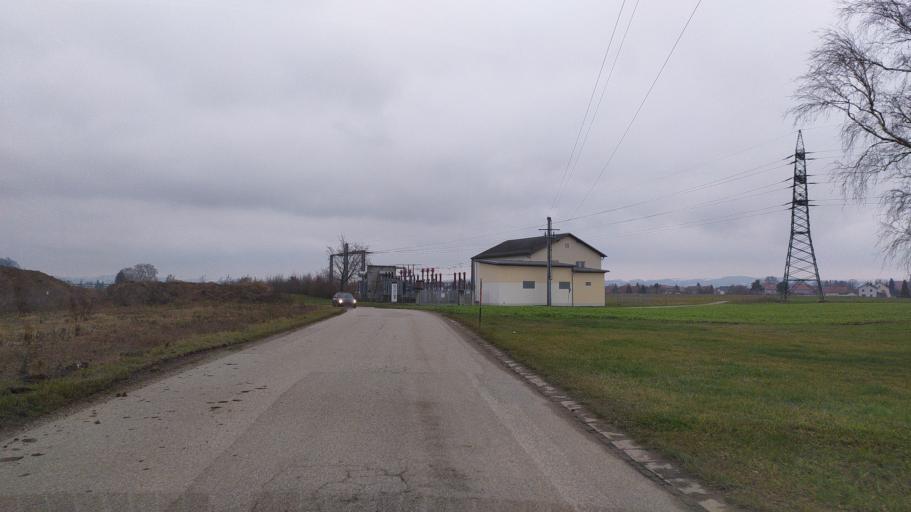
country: AT
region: Upper Austria
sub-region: Politischer Bezirk Urfahr-Umgebung
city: Feldkirchen an der Donau
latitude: 48.3015
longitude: 14.0074
